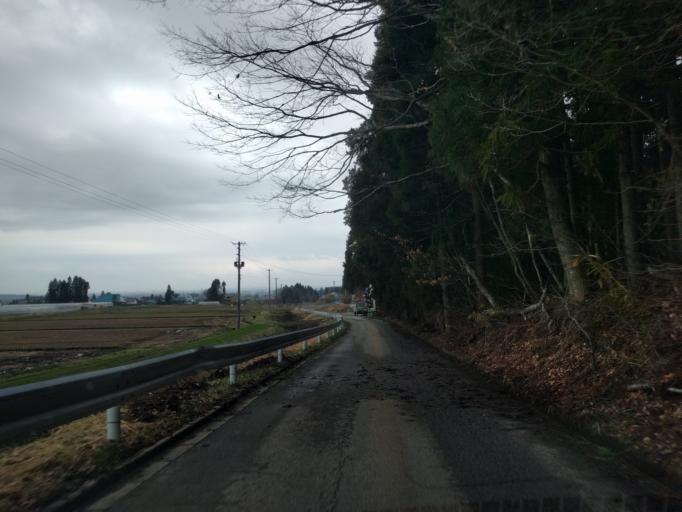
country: JP
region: Fukushima
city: Kitakata
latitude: 37.6726
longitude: 139.9178
